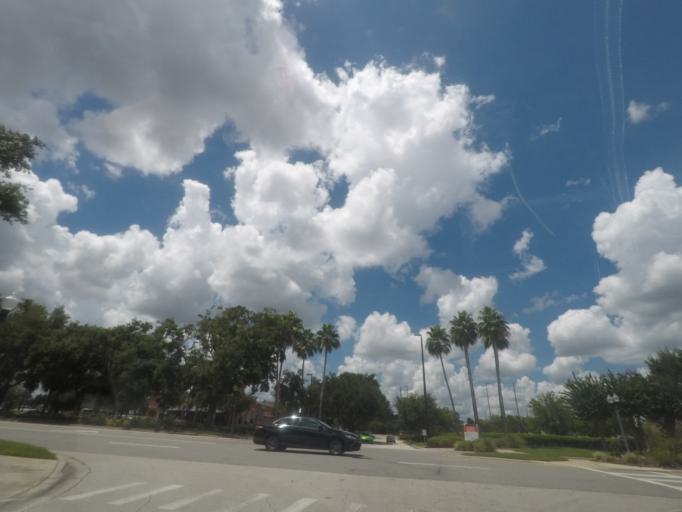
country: US
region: Florida
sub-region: Polk County
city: Citrus Ridge
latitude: 28.3480
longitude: -81.6125
